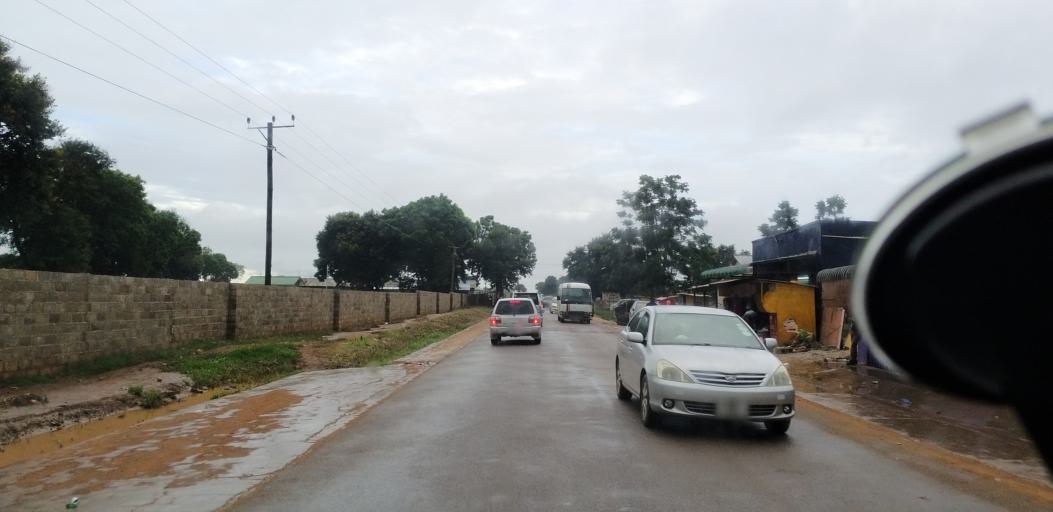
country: ZM
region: Lusaka
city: Lusaka
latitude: -15.5131
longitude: 28.3009
